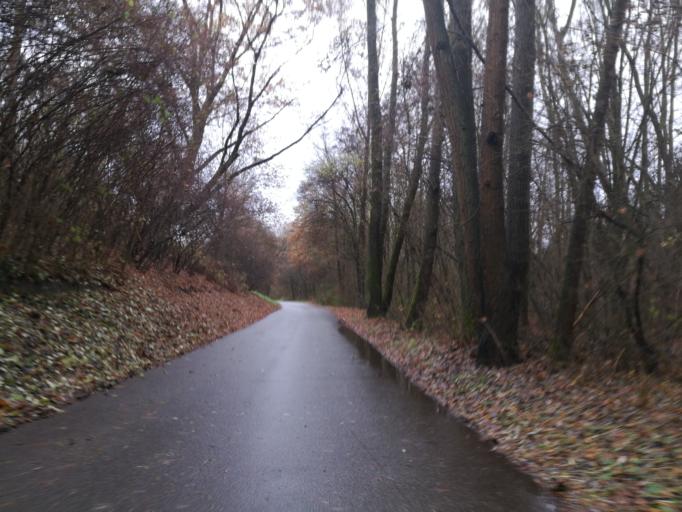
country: DE
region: Bavaria
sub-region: Regierungsbezirk Mittelfranken
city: Wetzendorf
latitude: 49.4640
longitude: 11.0351
